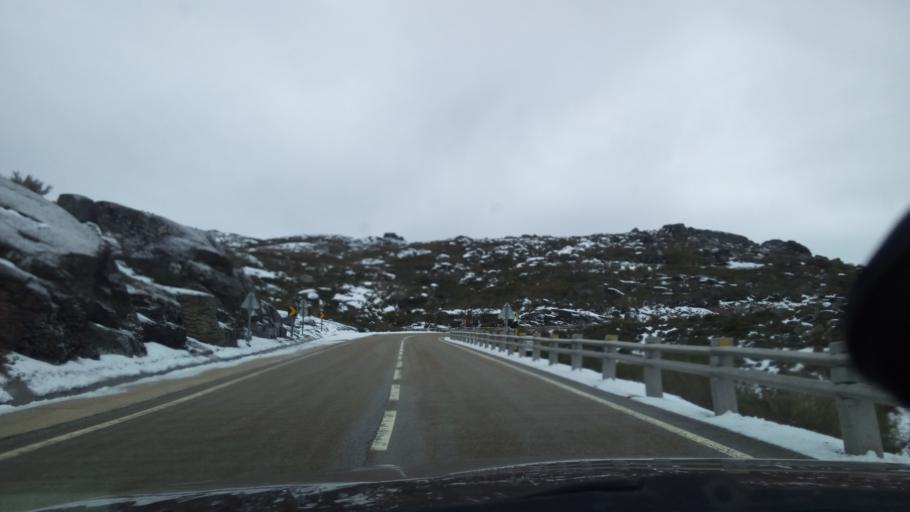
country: PT
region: Guarda
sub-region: Seia
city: Seia
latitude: 40.3575
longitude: -7.6657
